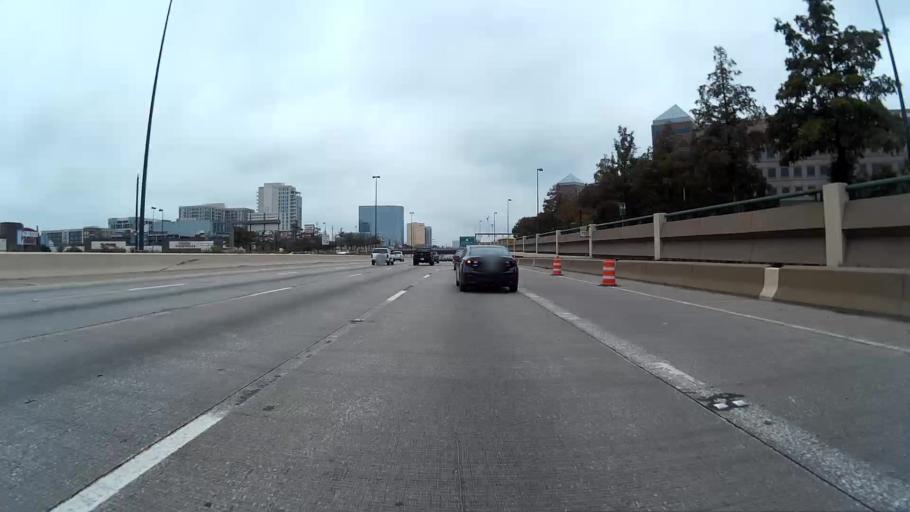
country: US
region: Texas
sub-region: Dallas County
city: University Park
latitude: 32.8745
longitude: -96.7704
